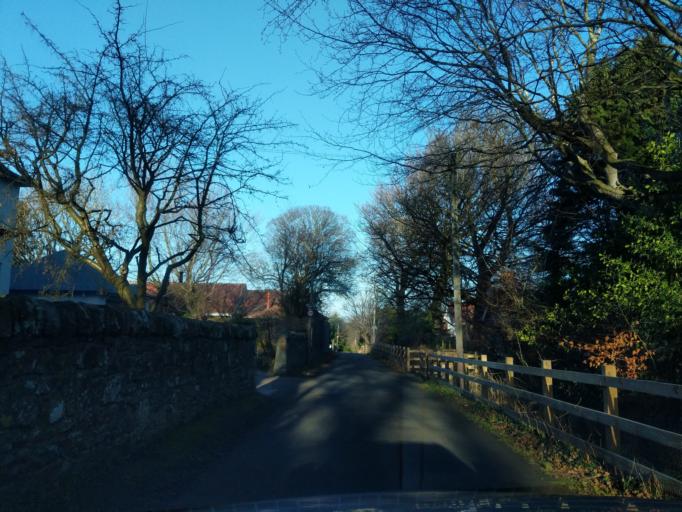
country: GB
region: Scotland
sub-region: Edinburgh
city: Colinton
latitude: 55.9013
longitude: -3.2642
